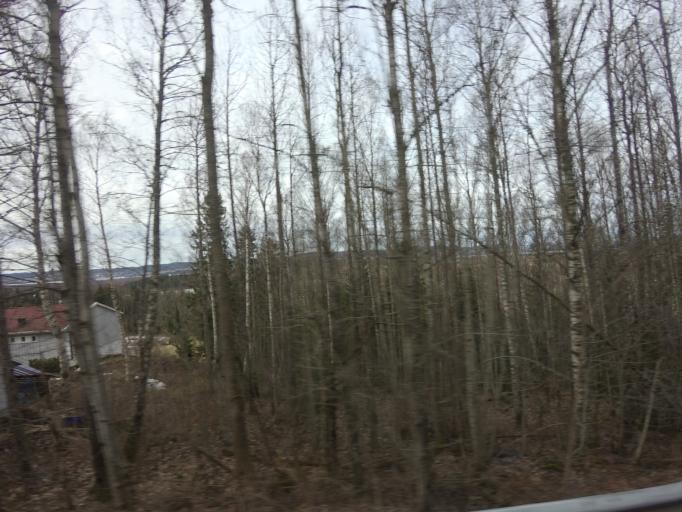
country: NO
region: Akershus
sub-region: Fet
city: Fetsund
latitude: 59.9057
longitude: 11.1807
